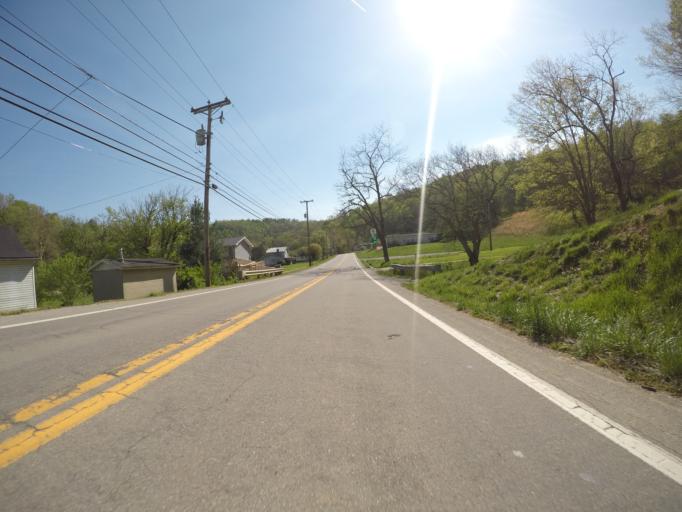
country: US
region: West Virginia
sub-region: Kanawha County
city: Clendenin
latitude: 38.5117
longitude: -81.3571
